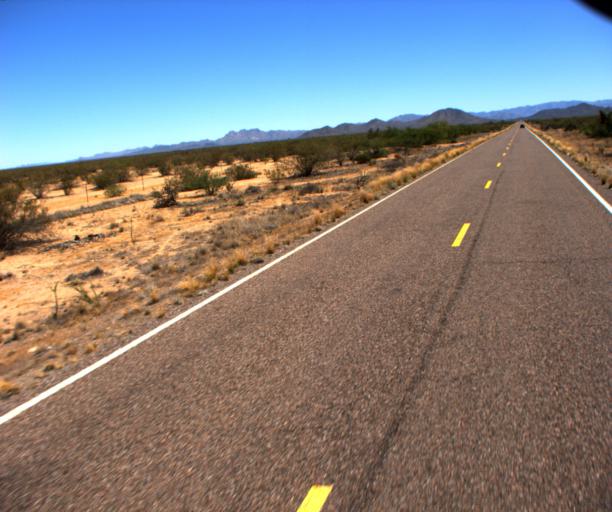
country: US
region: Arizona
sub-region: Yavapai County
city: Congress
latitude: 34.0470
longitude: -113.0627
